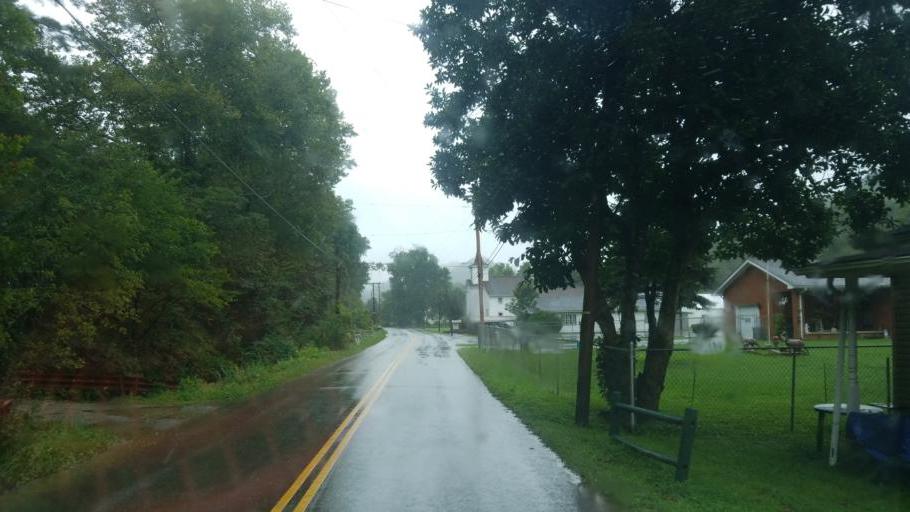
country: US
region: Ohio
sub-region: Scioto County
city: West Portsmouth
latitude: 38.7366
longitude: -83.0672
